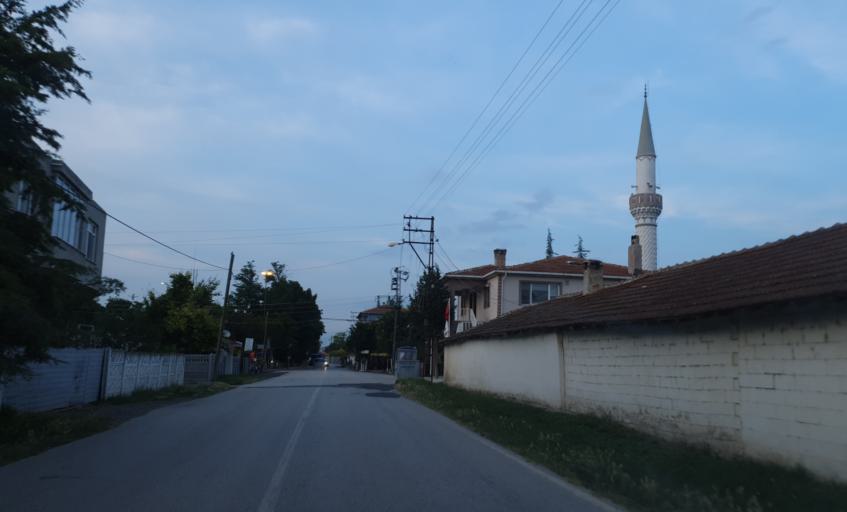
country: TR
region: Kirklareli
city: Buyukkaristiran
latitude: 41.3458
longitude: 27.6076
